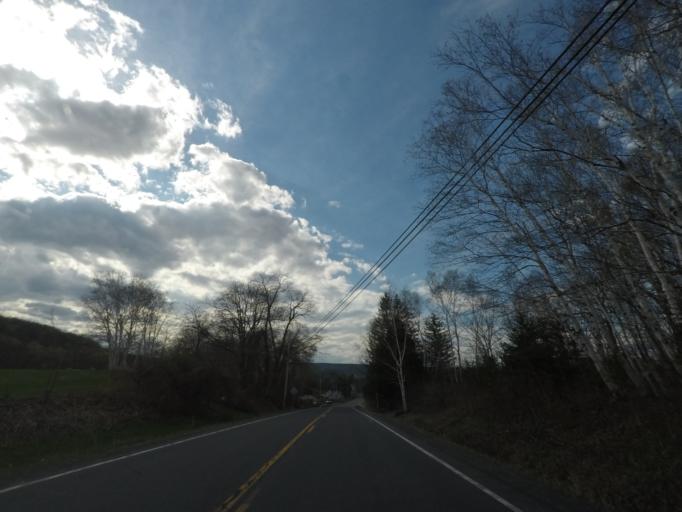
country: US
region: New York
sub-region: Albany County
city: Voorheesville
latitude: 42.5710
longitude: -73.9547
